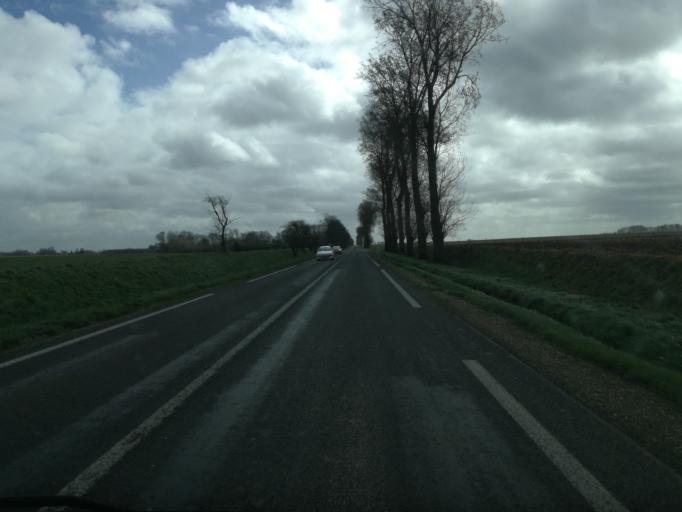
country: FR
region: Haute-Normandie
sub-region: Departement de la Seine-Maritime
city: Fauville-en-Caux
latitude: 49.6464
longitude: 0.6126
